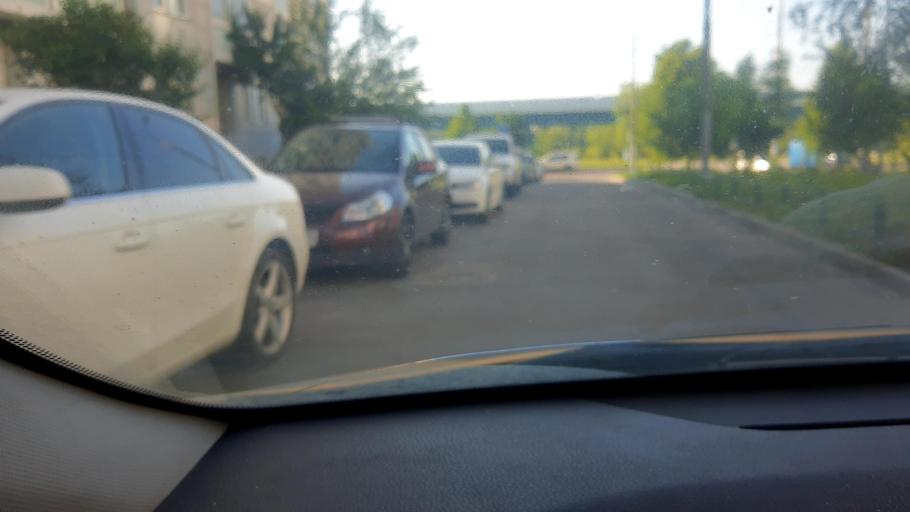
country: RU
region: Moskovskaya
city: Kommunarka
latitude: 55.5411
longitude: 37.5227
